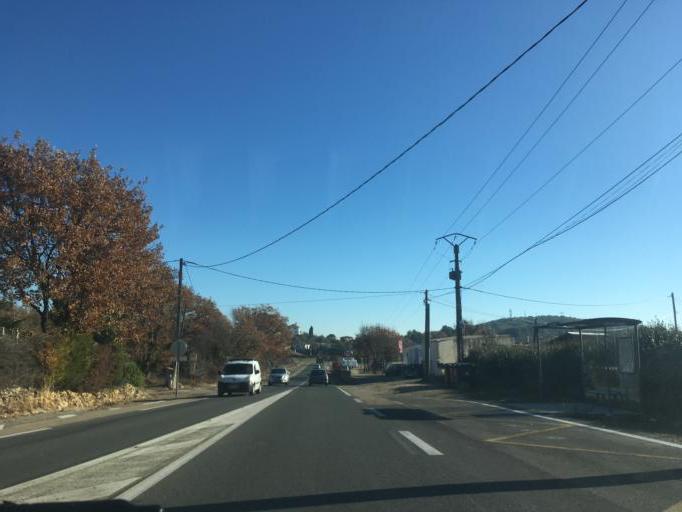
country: FR
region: Provence-Alpes-Cote d'Azur
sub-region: Departement du Var
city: Draguignan
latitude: 43.5279
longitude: 6.4312
